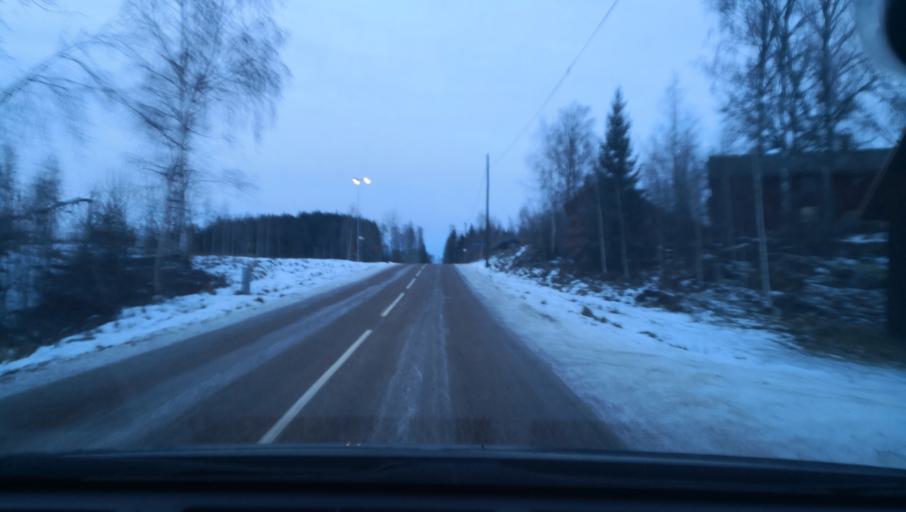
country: SE
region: Dalarna
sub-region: Avesta Kommun
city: Horndal
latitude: 60.1916
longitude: 16.4680
